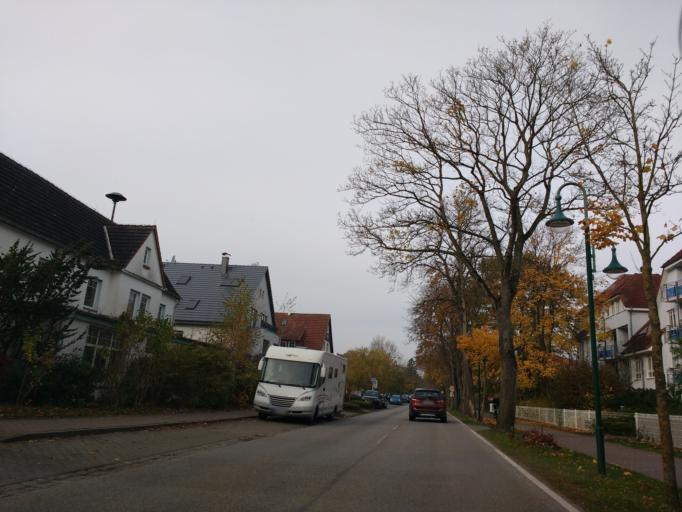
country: DE
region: Mecklenburg-Vorpommern
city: Ostseebad Boltenhagen
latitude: 53.9845
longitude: 11.2106
